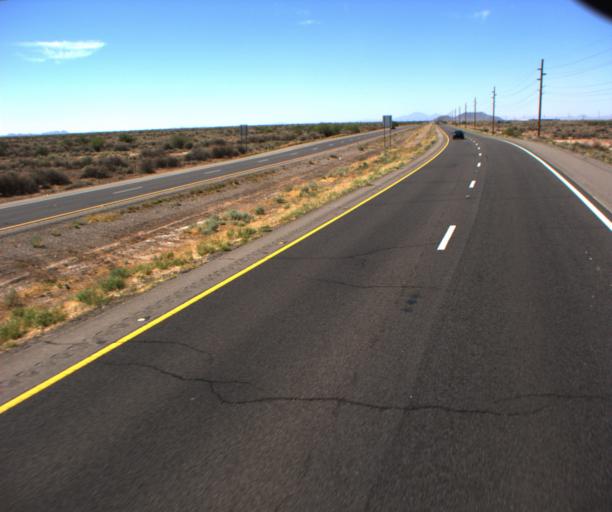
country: US
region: Arizona
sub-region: Maricopa County
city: Sun Lakes
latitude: 33.2472
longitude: -111.9797
